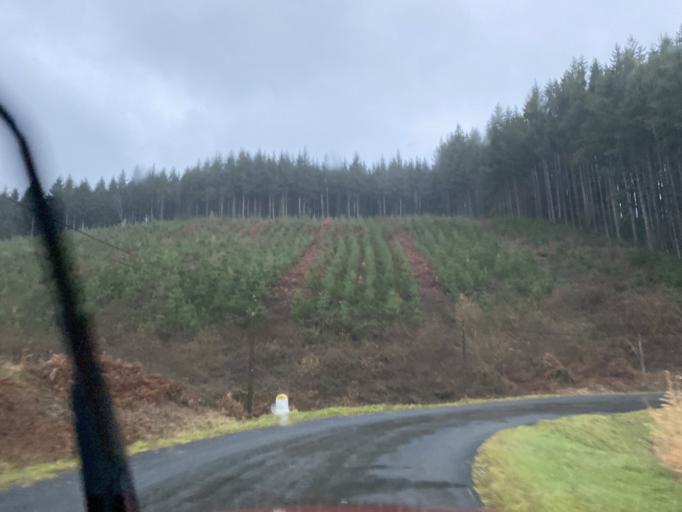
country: FR
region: Auvergne
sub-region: Departement du Puy-de-Dome
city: La Monnerie-le-Montel
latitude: 45.8448
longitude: 3.6062
